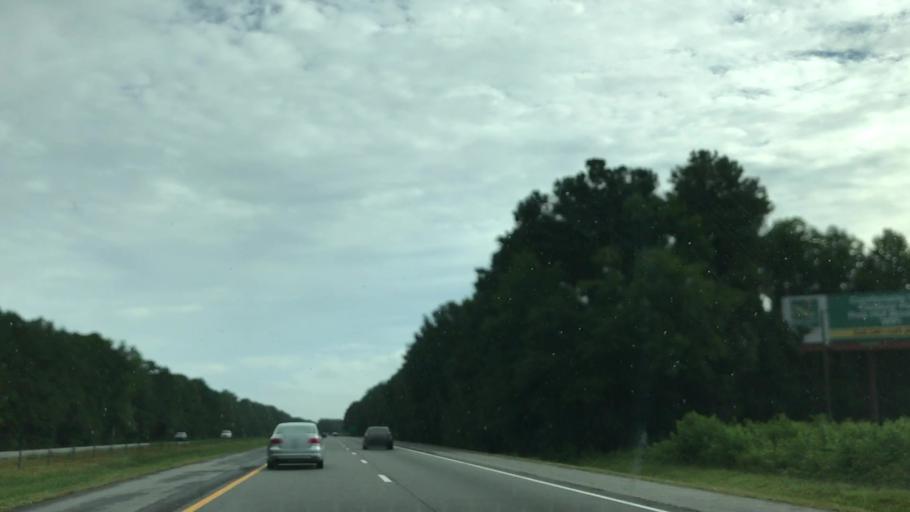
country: US
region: North Carolina
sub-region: Nash County
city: Red Oak
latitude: 36.0433
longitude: -77.8332
